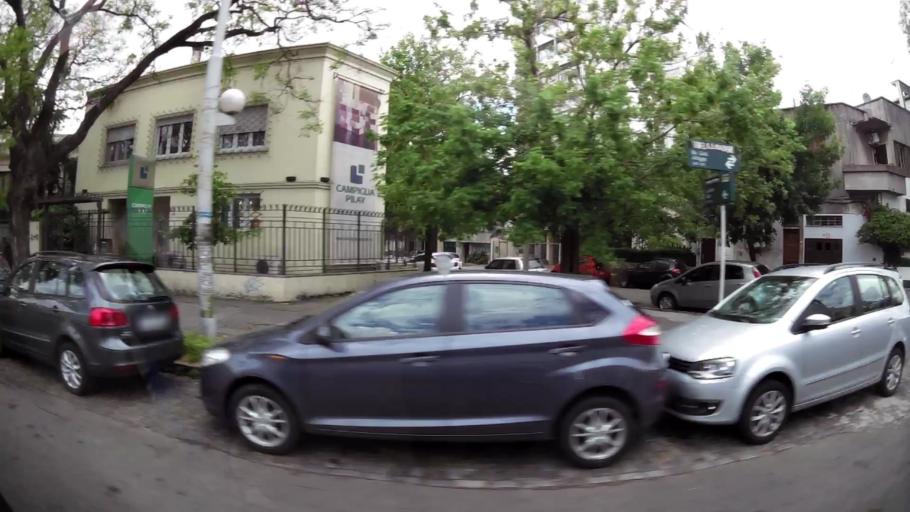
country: UY
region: Montevideo
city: Montevideo
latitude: -34.9204
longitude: -56.1620
